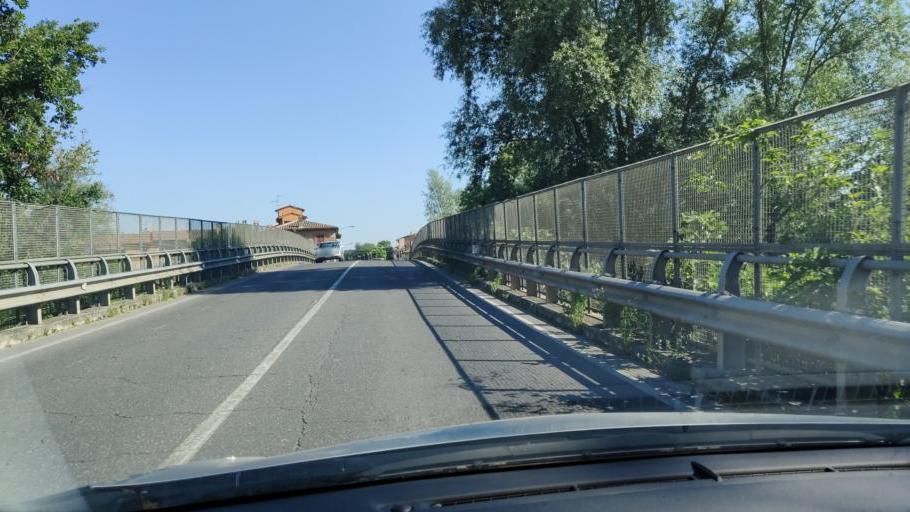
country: IT
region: Umbria
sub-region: Provincia di Perugia
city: Ponterio-Pian di Porto
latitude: 42.7973
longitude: 12.4099
